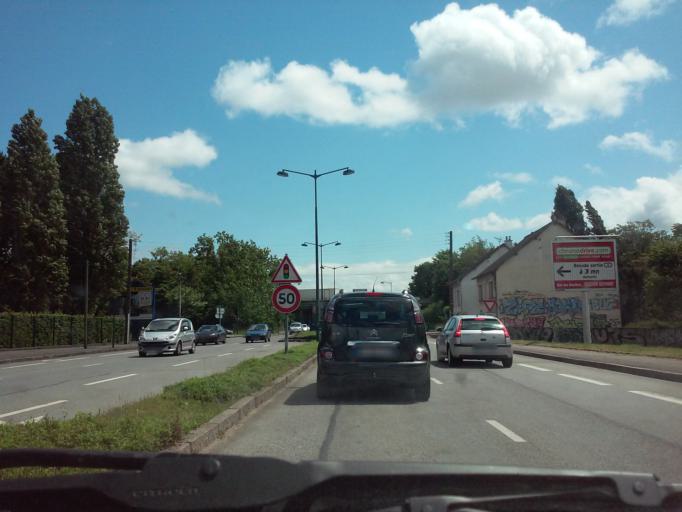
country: FR
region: Brittany
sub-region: Departement d'Ille-et-Vilaine
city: Chantepie
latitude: 48.0923
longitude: -1.6292
